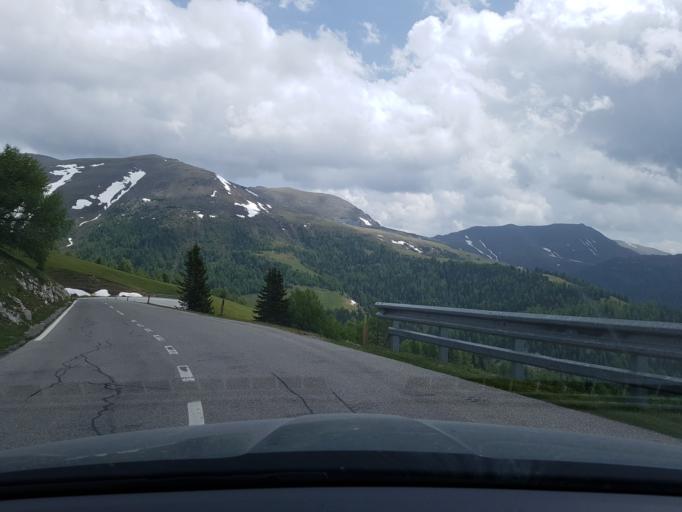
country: AT
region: Carinthia
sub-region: Politischer Bezirk Spittal an der Drau
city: Kleinkirchheim
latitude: 46.9274
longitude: 13.7571
